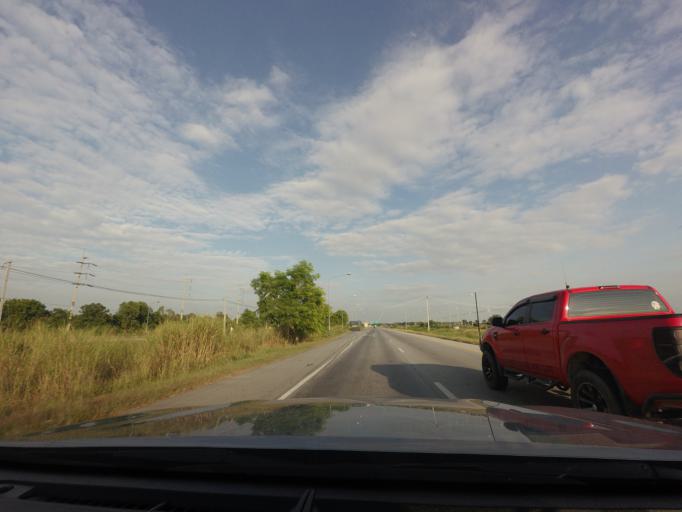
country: TH
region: Nakhon Sawan
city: Nakhon Sawan
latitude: 15.7684
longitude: 100.1126
